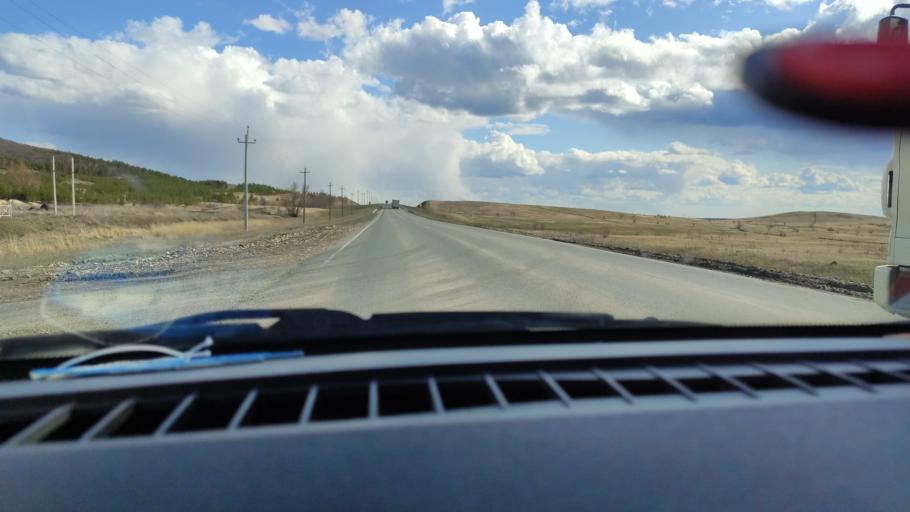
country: RU
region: Saratov
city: Alekseyevka
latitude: 52.3025
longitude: 47.9267
